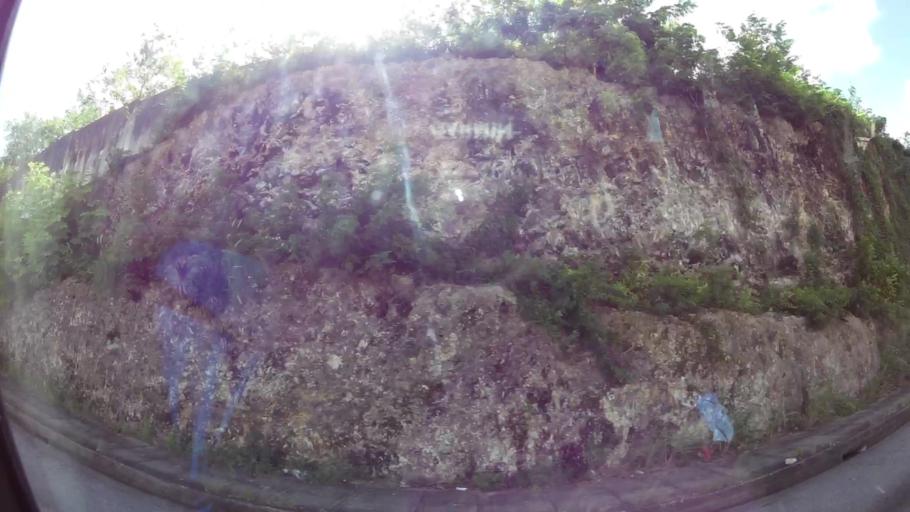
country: BB
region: Saint James
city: Holetown
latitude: 13.2025
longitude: -59.6124
